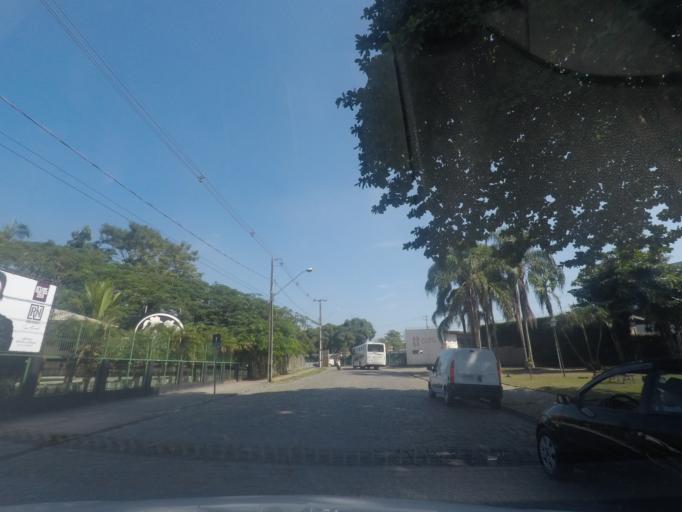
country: BR
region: Parana
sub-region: Paranagua
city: Paranagua
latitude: -25.5240
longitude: -48.5112
